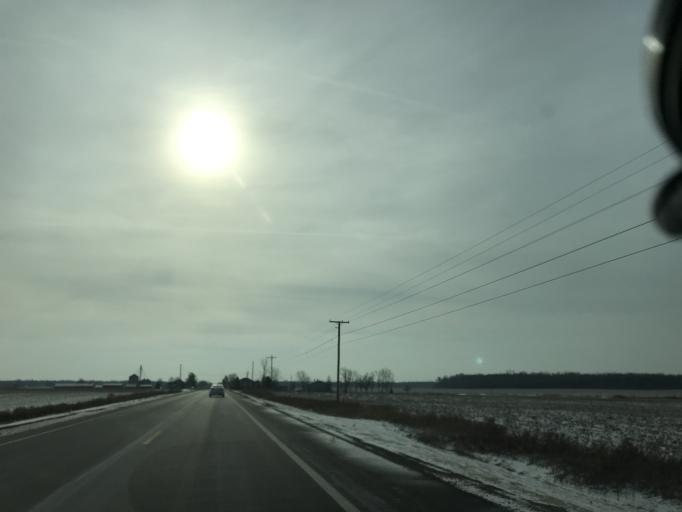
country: US
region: Michigan
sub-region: Ionia County
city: Lake Odessa
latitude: 42.8312
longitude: -85.0748
